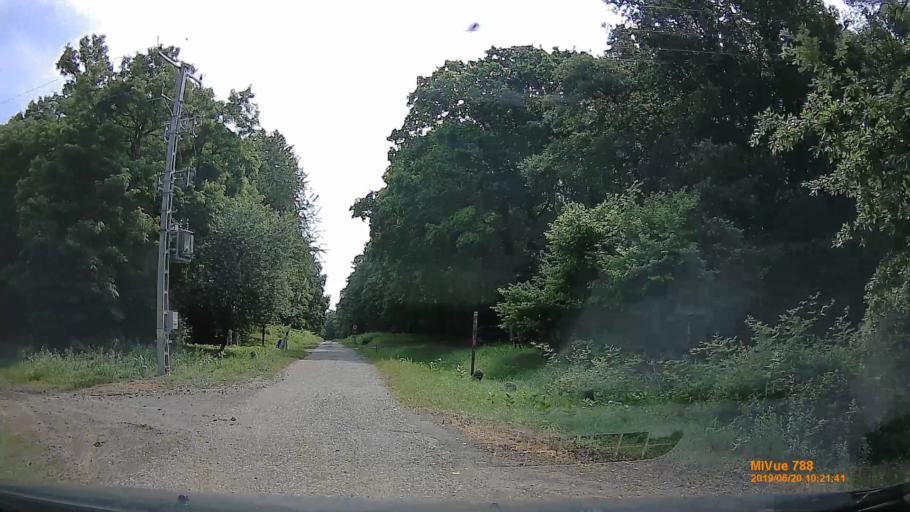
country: HU
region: Baranya
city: Mecseknadasd
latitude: 46.2092
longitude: 18.4784
